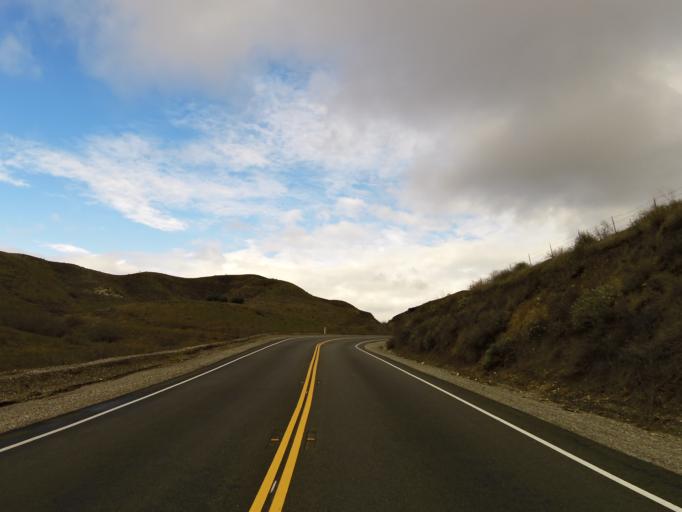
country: US
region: California
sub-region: Ventura County
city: Moorpark
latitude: 34.3349
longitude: -118.9018
